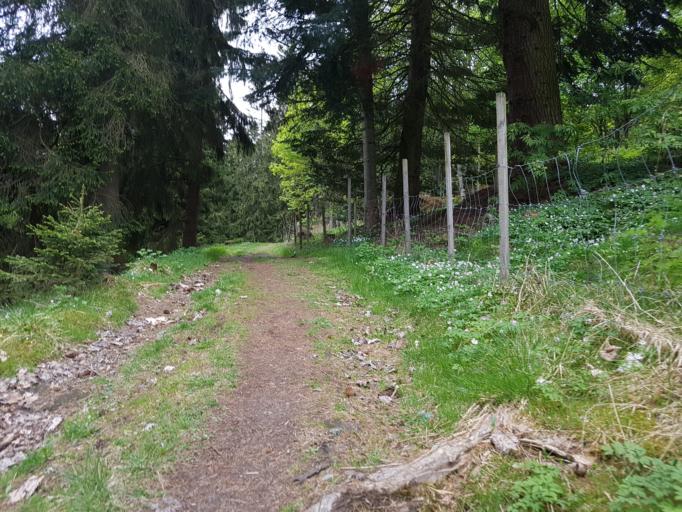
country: NO
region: Nord-Trondelag
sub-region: Levanger
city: Levanger
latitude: 63.7425
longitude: 11.2705
